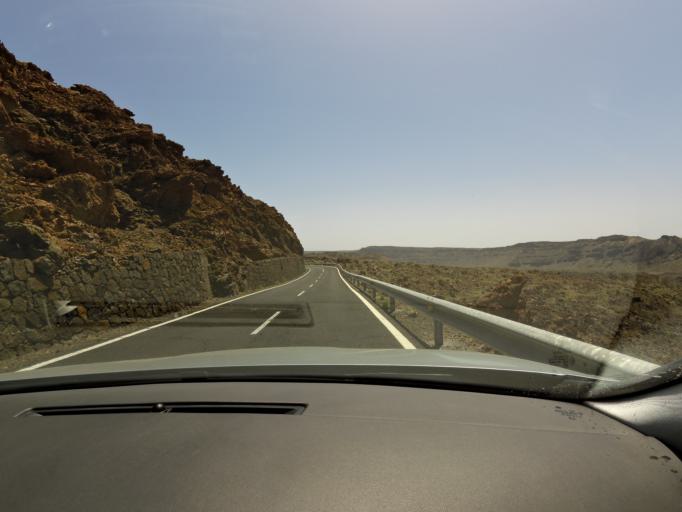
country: ES
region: Canary Islands
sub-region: Provincia de Santa Cruz de Tenerife
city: Vilaflor
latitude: 28.2590
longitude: -16.5989
